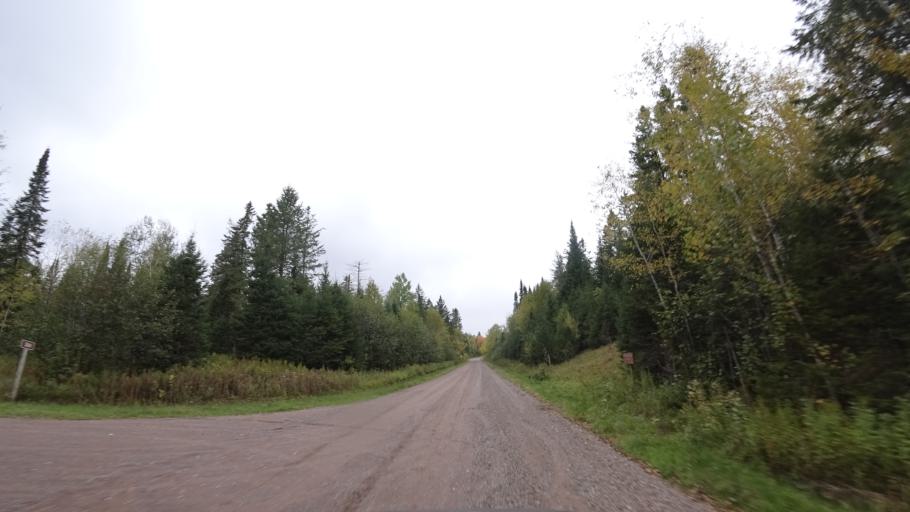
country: US
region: Wisconsin
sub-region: Sawyer County
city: Little Round Lake
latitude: 45.9770
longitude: -90.9924
